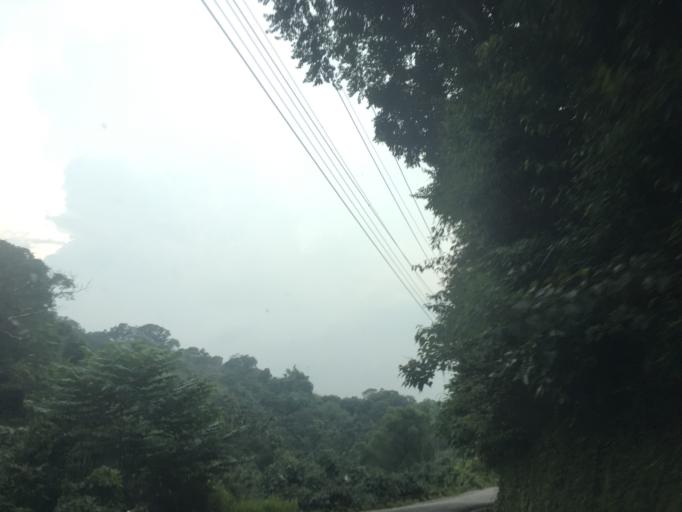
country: TW
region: Taiwan
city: Fengyuan
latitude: 24.1869
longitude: 120.7835
